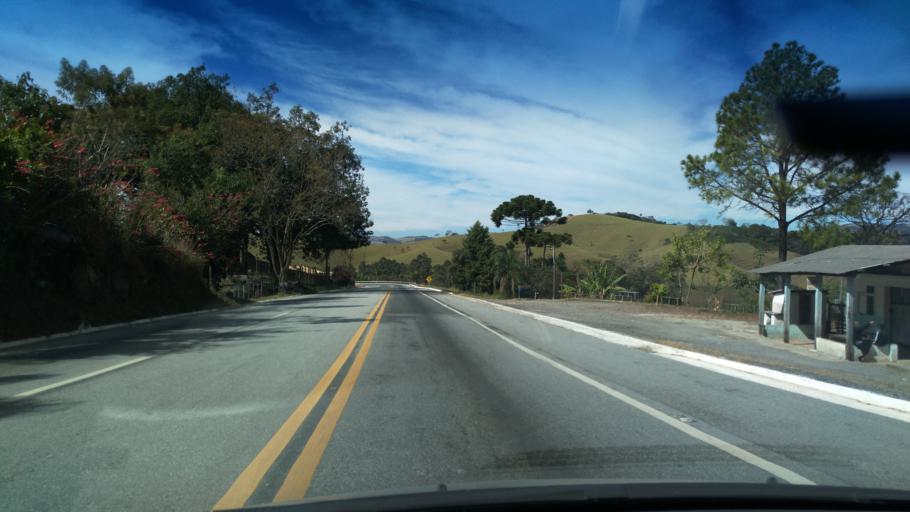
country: BR
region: Minas Gerais
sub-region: Borda Da Mata
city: Borda da Mata
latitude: -22.1340
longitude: -46.1627
